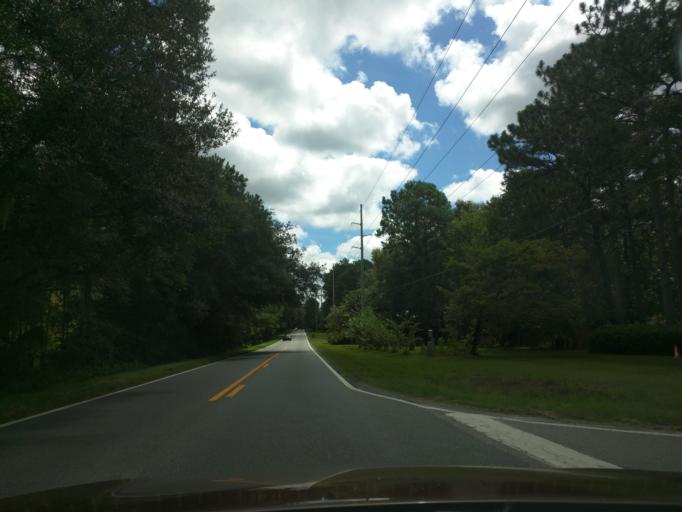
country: US
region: Florida
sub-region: Leon County
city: Tallahassee
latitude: 30.5596
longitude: -84.1874
